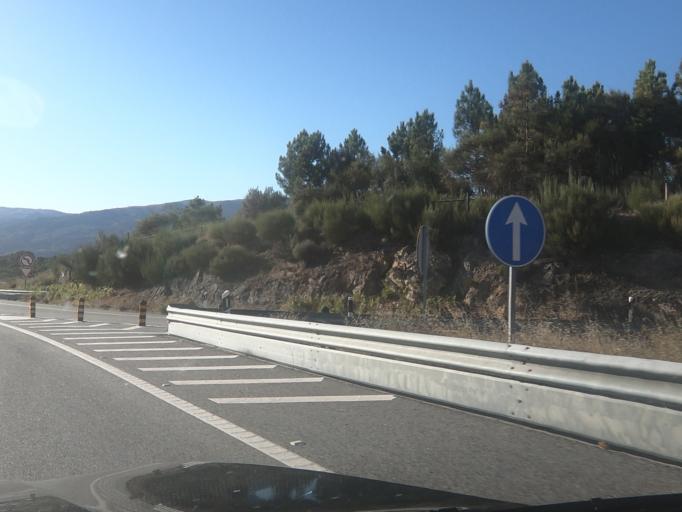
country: PT
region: Vila Real
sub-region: Vila Real
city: Vila Real
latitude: 41.3289
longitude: -7.6748
